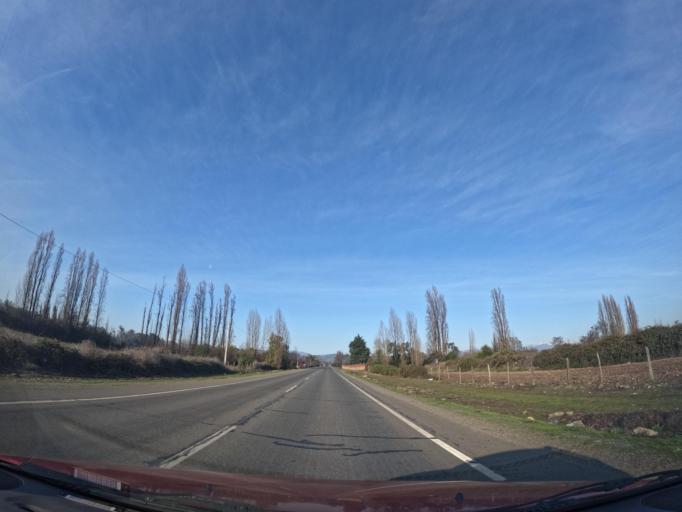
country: CL
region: Maule
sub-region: Provincia de Linares
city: Colbun
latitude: -35.6293
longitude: -71.4445
